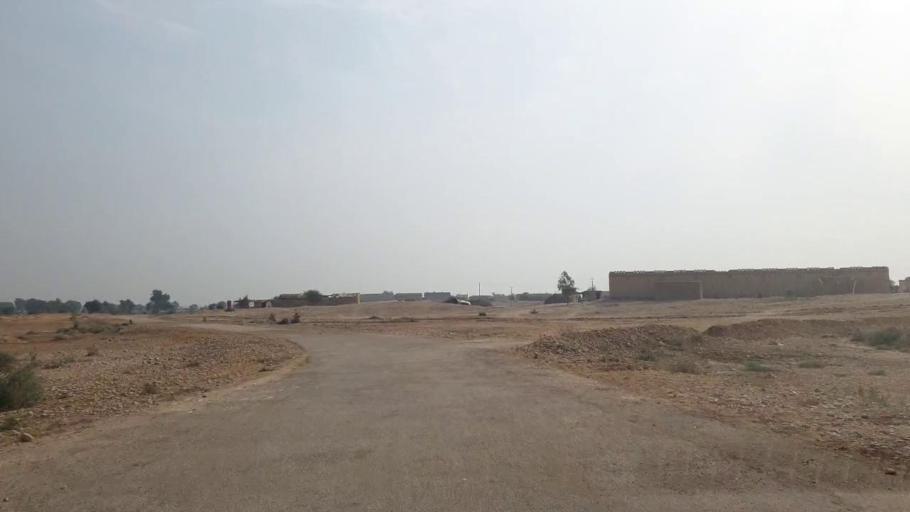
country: PK
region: Sindh
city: Sann
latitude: 26.0052
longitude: 68.1398
